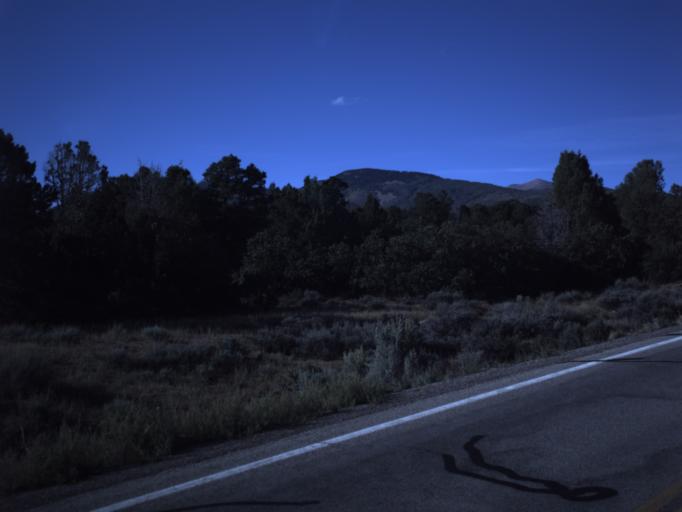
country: US
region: Utah
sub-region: Grand County
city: Moab
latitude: 38.3291
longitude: -109.2252
